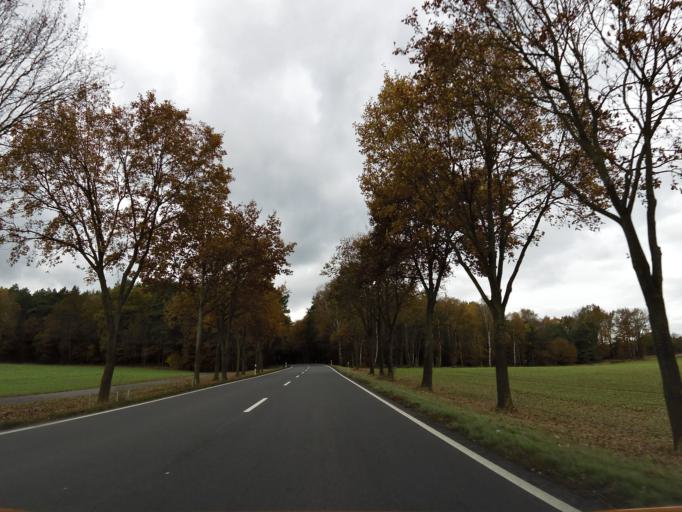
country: DE
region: Lower Saxony
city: Schnega
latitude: 52.9172
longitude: 10.8855
